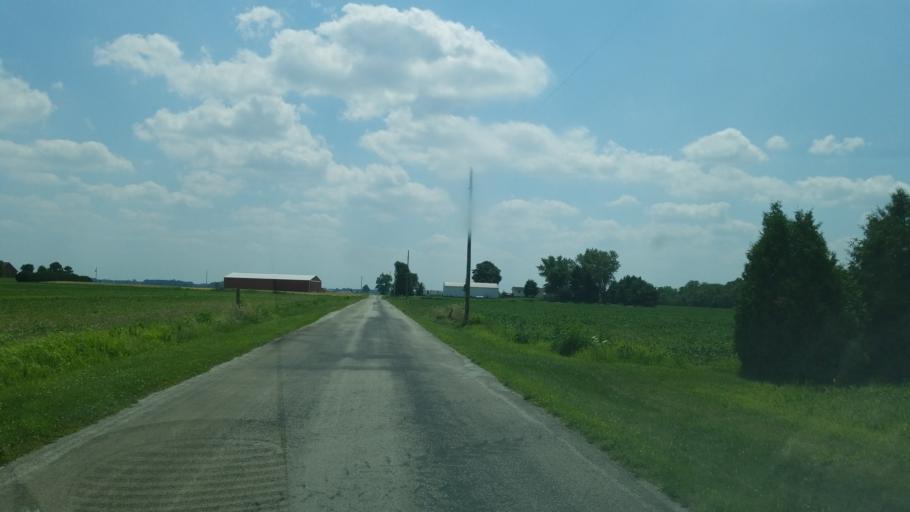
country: US
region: Ohio
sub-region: Seneca County
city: Fostoria
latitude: 41.2024
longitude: -83.5163
